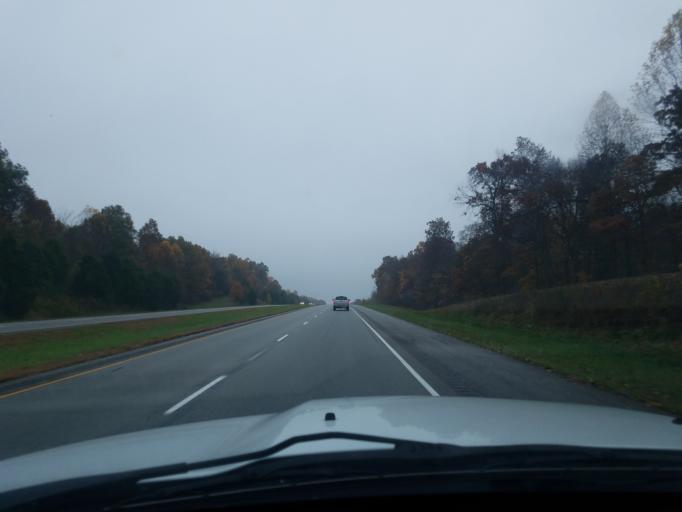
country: US
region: Kentucky
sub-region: Hardin County
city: Elizabethtown
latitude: 37.6380
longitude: -85.8340
